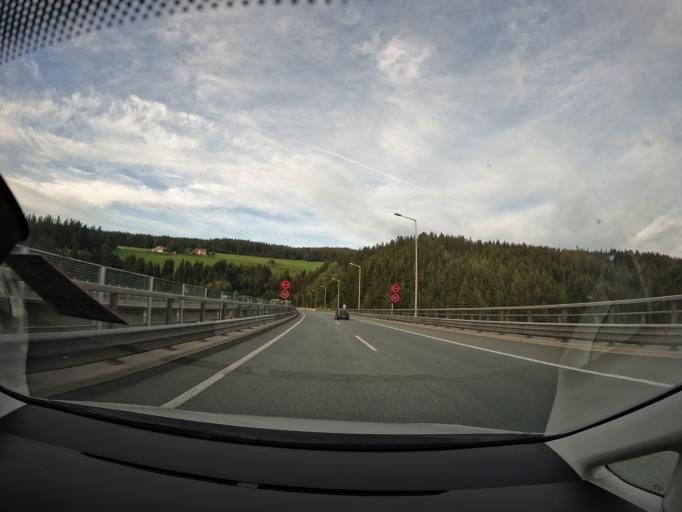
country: AT
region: Styria
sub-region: Politischer Bezirk Voitsberg
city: Pack
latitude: 46.9415
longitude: 15.0019
